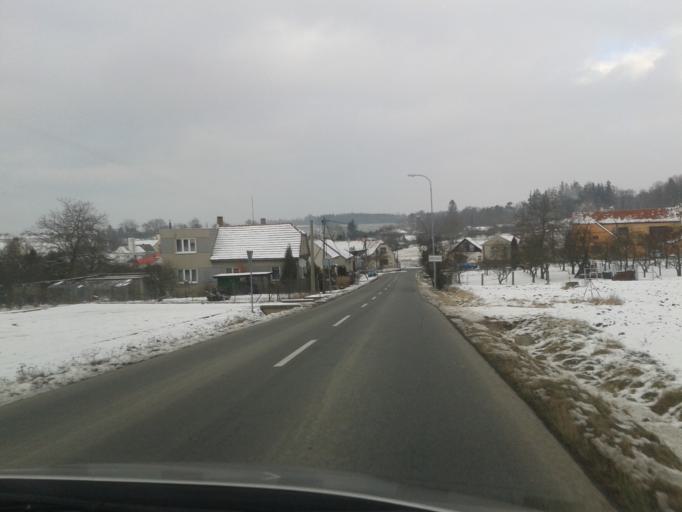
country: CZ
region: Olomoucky
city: Konice
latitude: 49.6049
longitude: 16.8925
